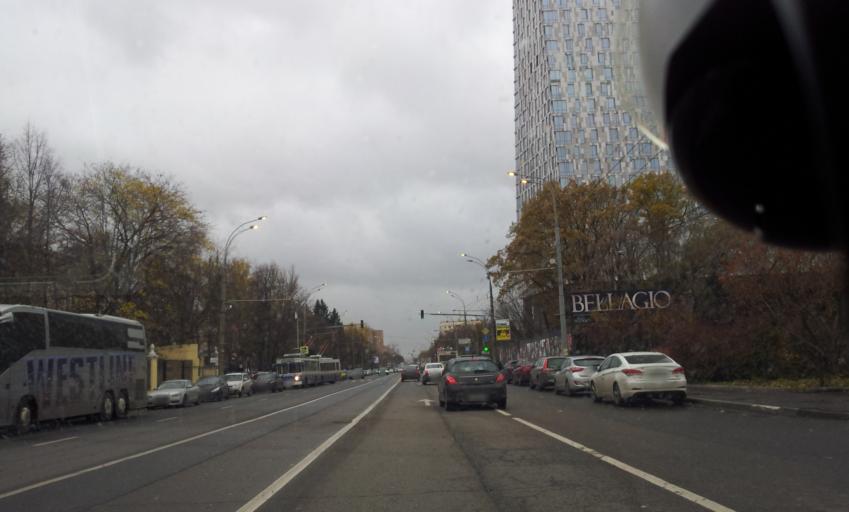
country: RU
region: Moscow
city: Vorob'yovo
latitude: 55.7243
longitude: 37.5308
